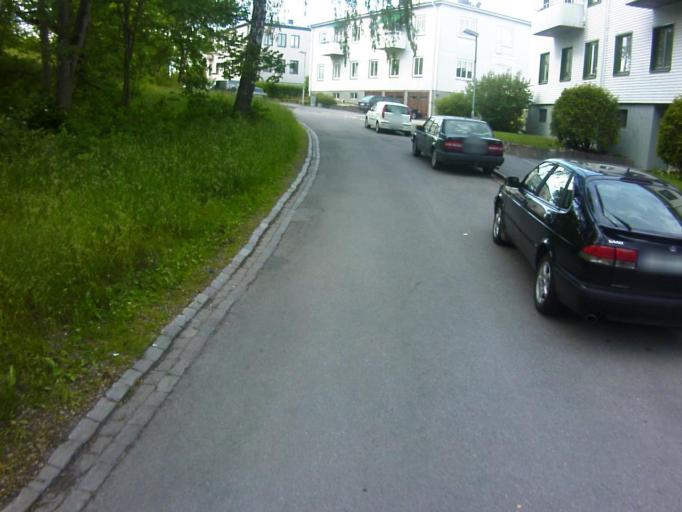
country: SE
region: Soedermanland
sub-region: Eskilstuna Kommun
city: Eskilstuna
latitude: 59.3637
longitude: 16.5064
